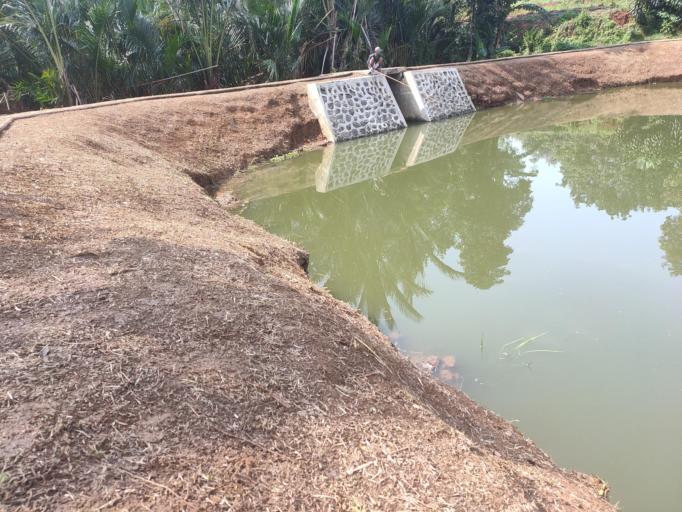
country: ID
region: West Java
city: Ciampea
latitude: -6.4856
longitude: 106.6608
